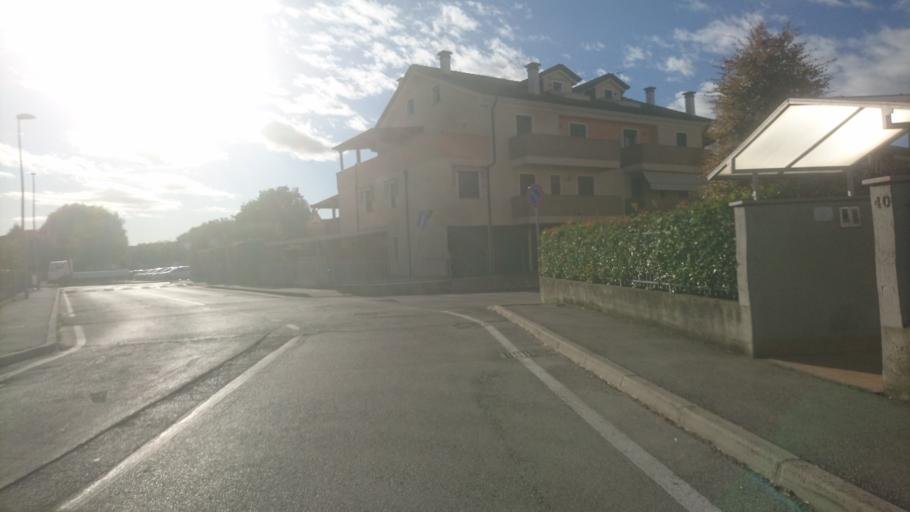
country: IT
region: Veneto
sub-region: Provincia di Padova
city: Mandriola-Sant'Agostino
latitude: 45.3488
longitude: 11.8570
